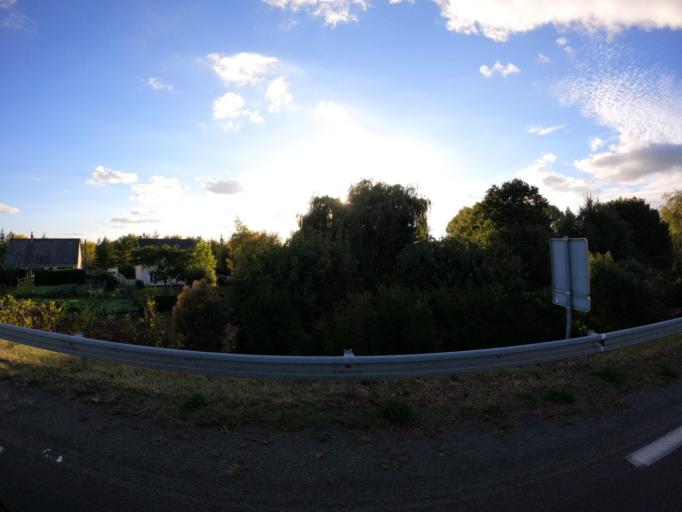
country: FR
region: Pays de la Loire
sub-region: Departement de Maine-et-Loire
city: Brissac-Quince
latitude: 47.3688
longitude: -0.4585
